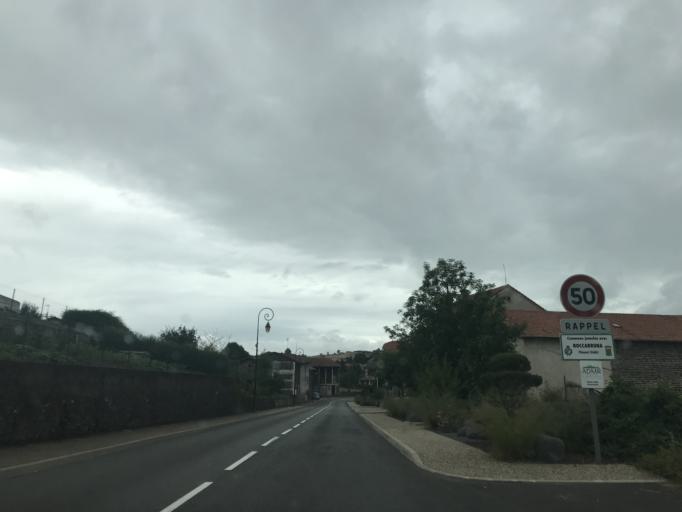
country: FR
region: Auvergne
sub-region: Departement de la Haute-Loire
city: Saint-Paulien
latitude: 45.1308
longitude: 3.8176
